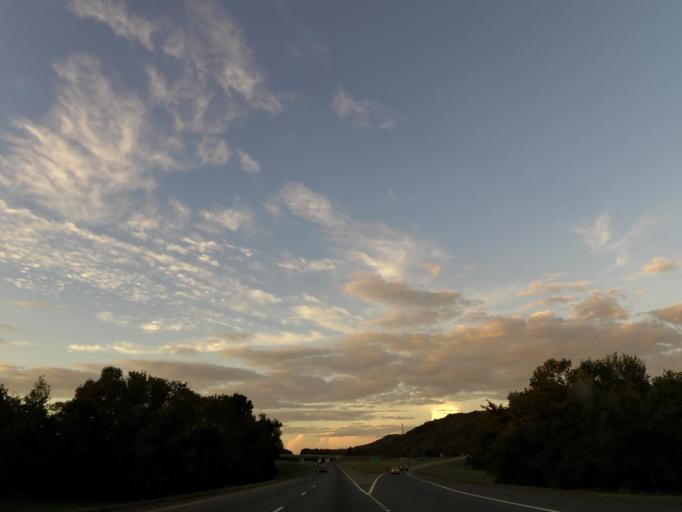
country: US
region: Tennessee
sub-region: McMinn County
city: Athens
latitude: 35.5441
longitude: -84.5697
